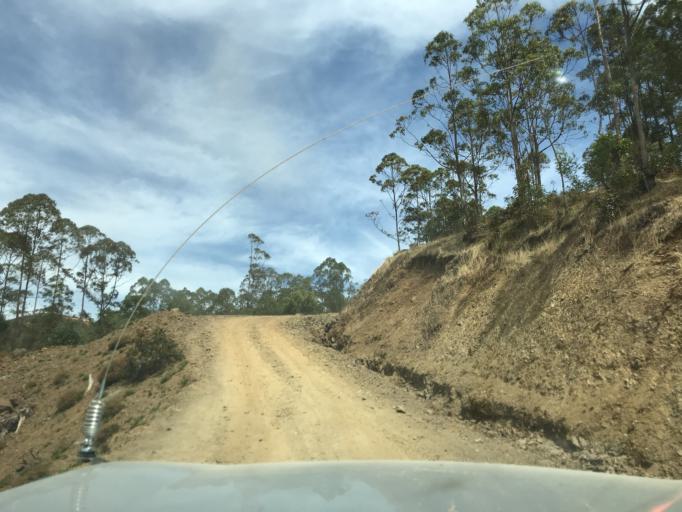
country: TL
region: Ainaro
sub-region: Ainaro
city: Ainaro
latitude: -8.8774
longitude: 125.5318
